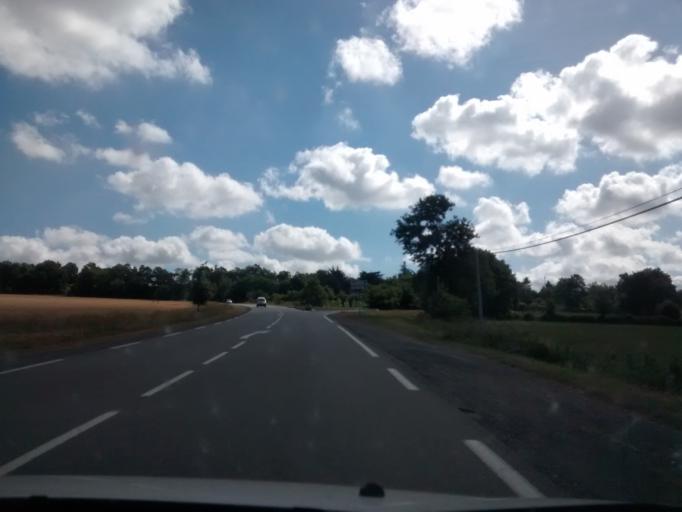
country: FR
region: Brittany
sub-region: Departement d'Ille-et-Vilaine
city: Bain-de-Bretagne
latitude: 47.8431
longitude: -1.7099
